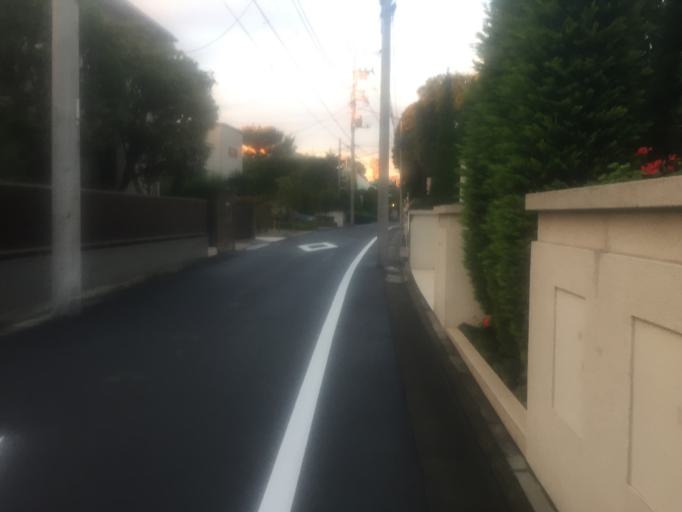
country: JP
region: Kanagawa
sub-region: Kawasaki-shi
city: Kawasaki
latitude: 35.5985
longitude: 139.6639
